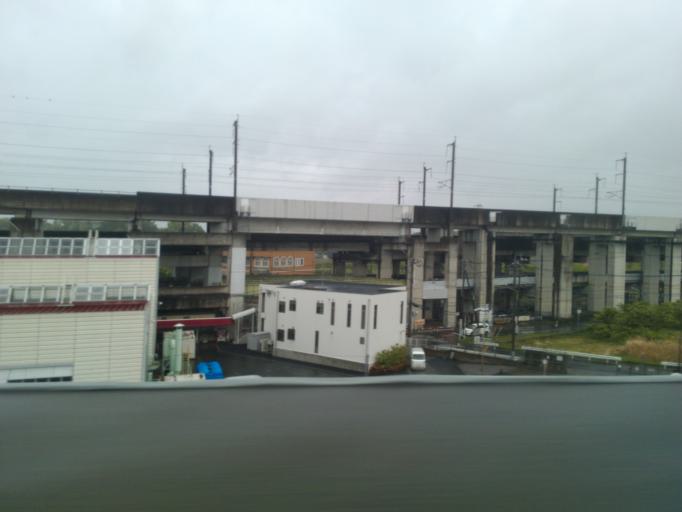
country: JP
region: Saitama
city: Ageoshimo
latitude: 35.9803
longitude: 139.6258
